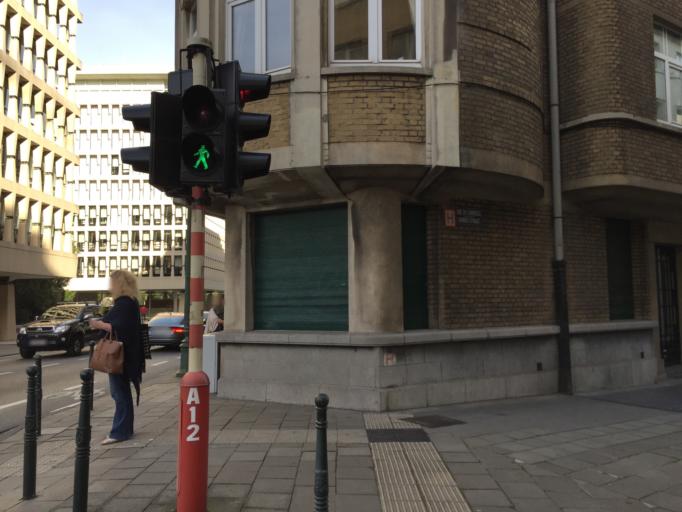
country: BE
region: Brussels Capital
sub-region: Bruxelles-Capitale
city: Brussels
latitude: 50.8394
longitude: 4.3669
